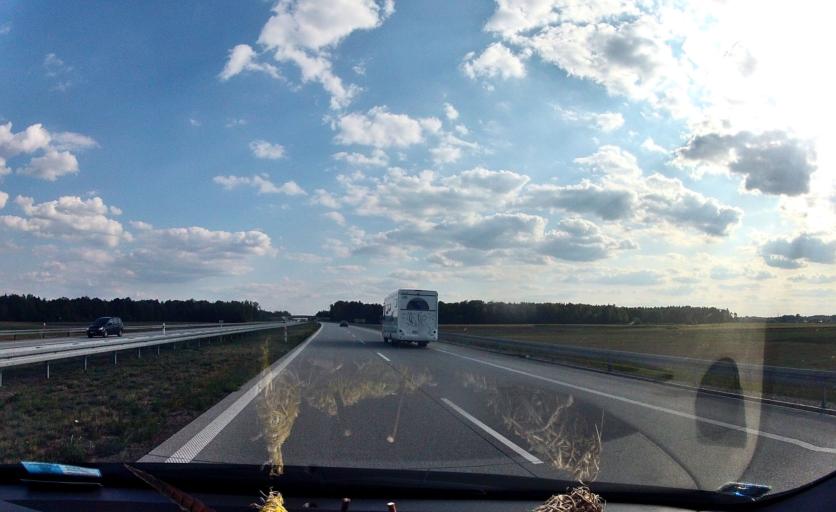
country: PL
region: Lodz Voivodeship
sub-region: Powiat sieradzki
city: Zloczew
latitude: 51.4466
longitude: 18.6460
